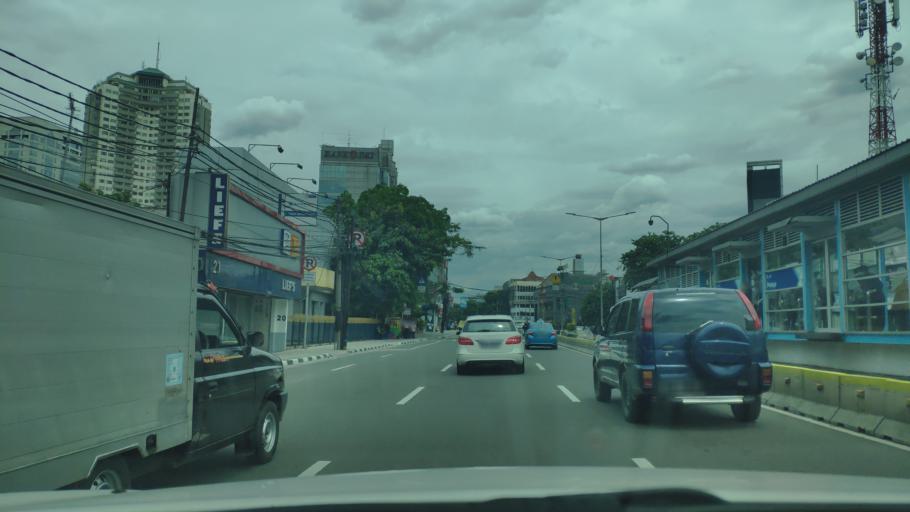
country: ID
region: Jakarta Raya
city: Jakarta
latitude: -6.1700
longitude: 106.8168
